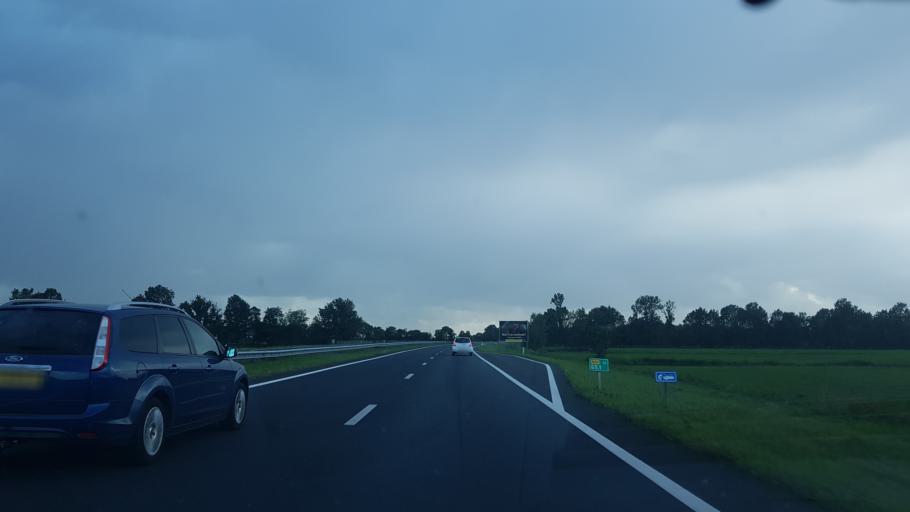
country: NL
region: Friesland
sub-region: Gemeente Smallingerland
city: Oudega
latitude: 53.1448
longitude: 6.0027
